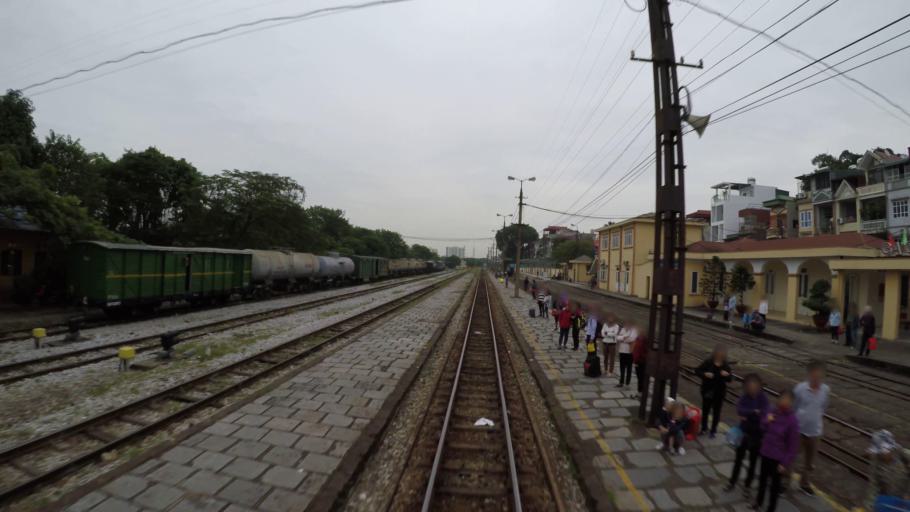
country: VN
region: Ha Noi
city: Trau Quy
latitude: 21.0332
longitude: 105.9067
